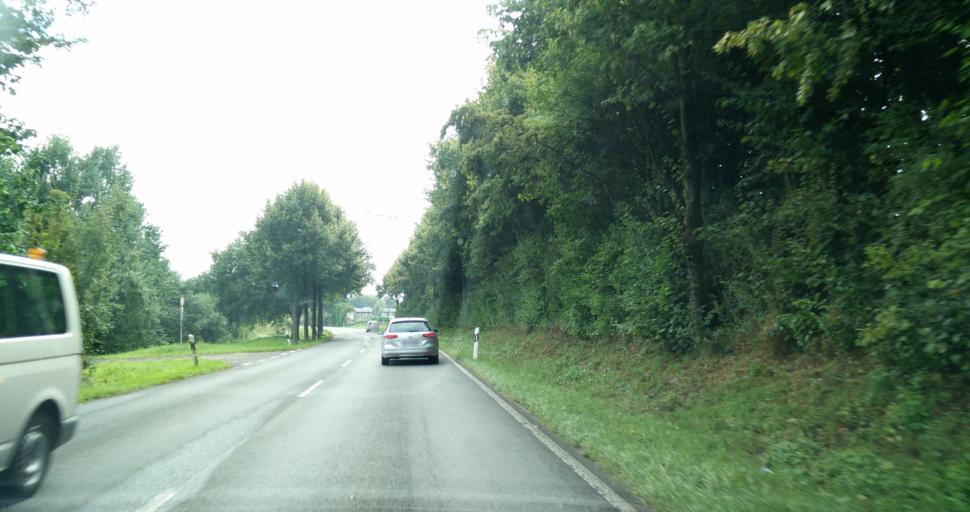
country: DE
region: North Rhine-Westphalia
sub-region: Regierungsbezirk Dusseldorf
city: Mettmann
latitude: 51.2410
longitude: 7.0067
